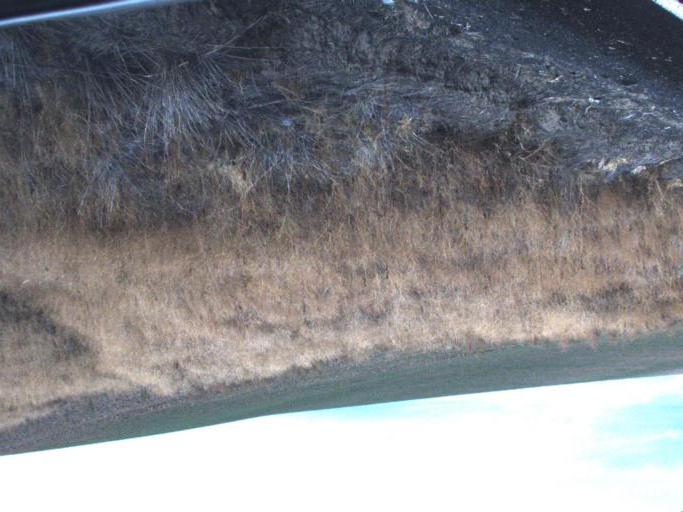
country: US
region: Washington
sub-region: Okanogan County
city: Coulee Dam
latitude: 47.8537
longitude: -118.7179
